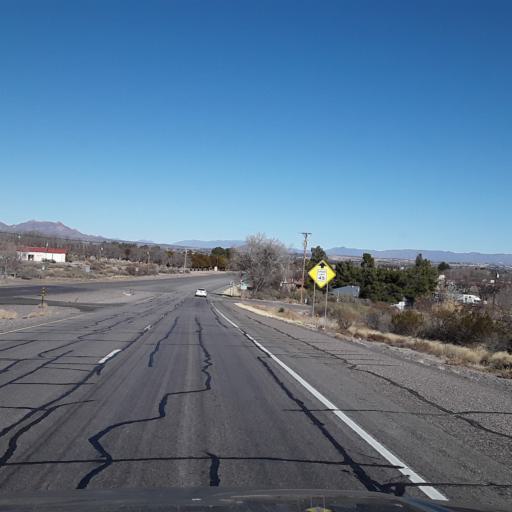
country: US
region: New Mexico
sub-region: Dona Ana County
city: Mesilla
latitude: 32.2974
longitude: -106.8559
